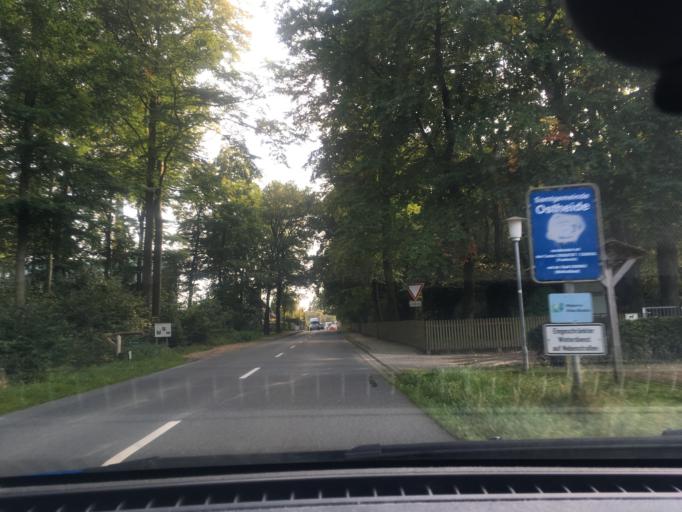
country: DE
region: Lower Saxony
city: Barendorf
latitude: 53.2314
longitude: 10.5271
